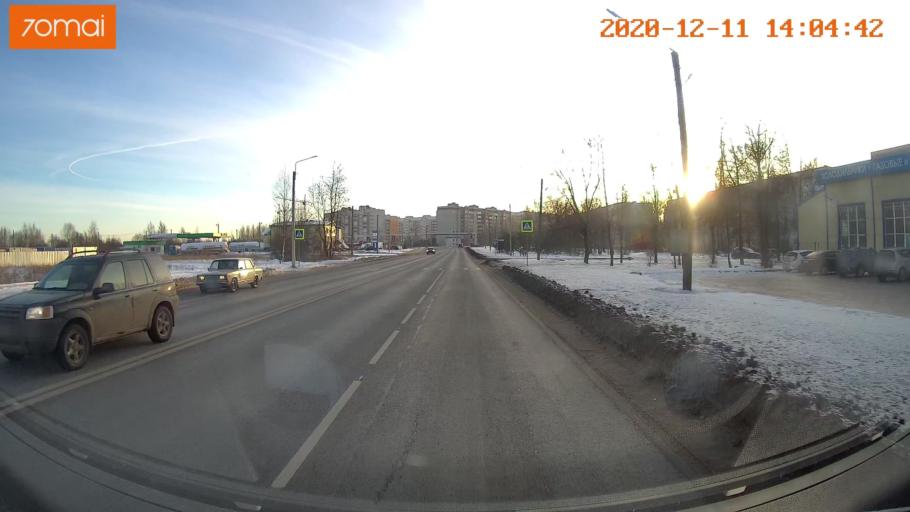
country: RU
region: Kostroma
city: Oktyabr'skiy
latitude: 57.7528
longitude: 41.0164
